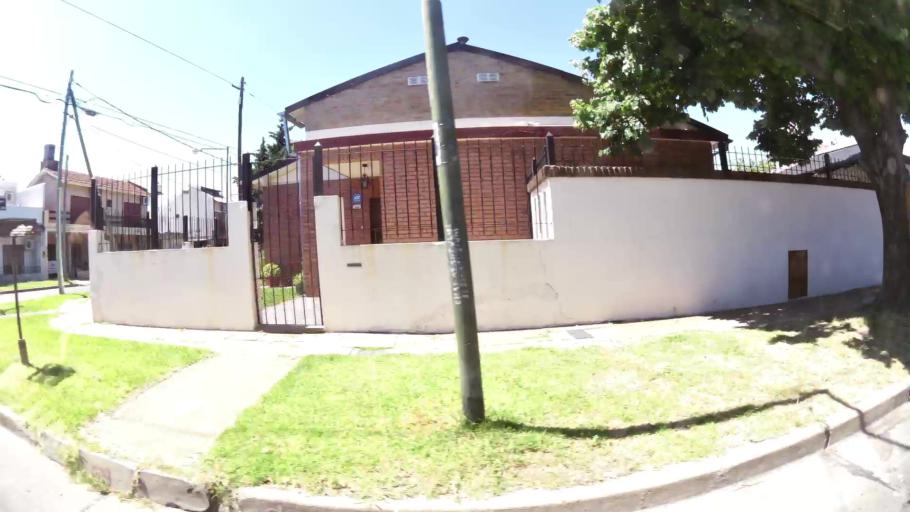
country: AR
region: Buenos Aires
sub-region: Partido de Vicente Lopez
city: Olivos
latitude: -34.5169
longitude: -58.5380
